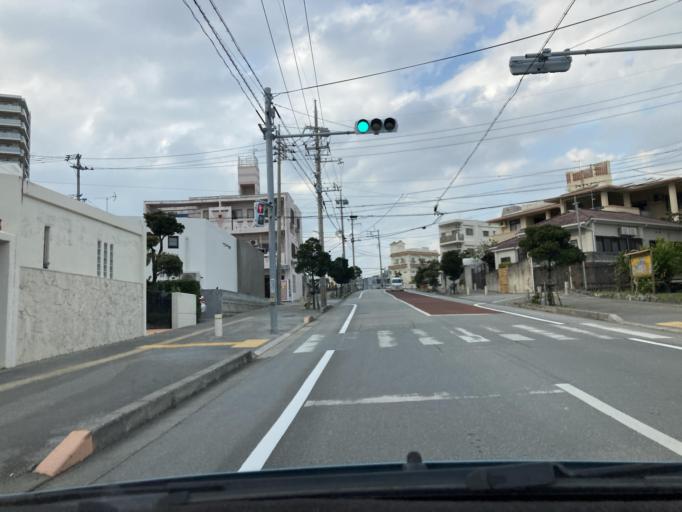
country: JP
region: Okinawa
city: Tomigusuku
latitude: 26.1958
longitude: 127.7333
